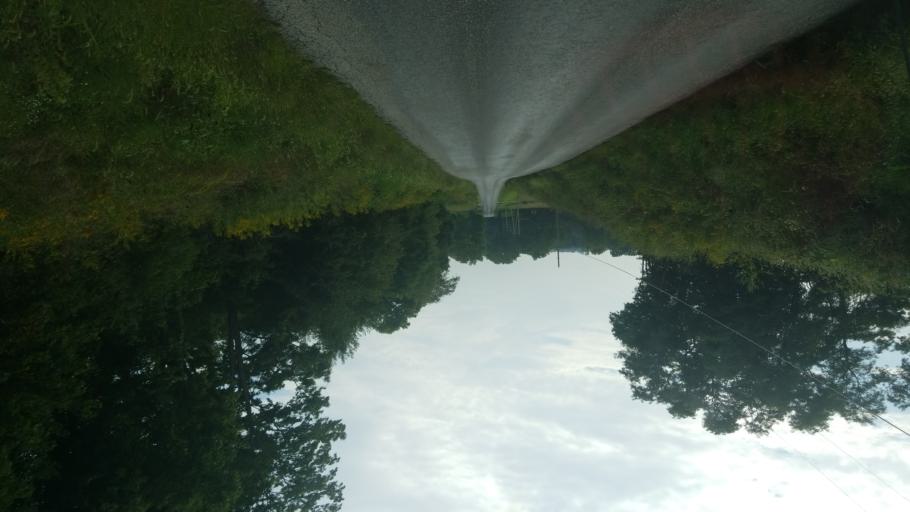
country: US
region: Ohio
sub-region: Wayne County
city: Wooster
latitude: 40.9011
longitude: -81.9951
